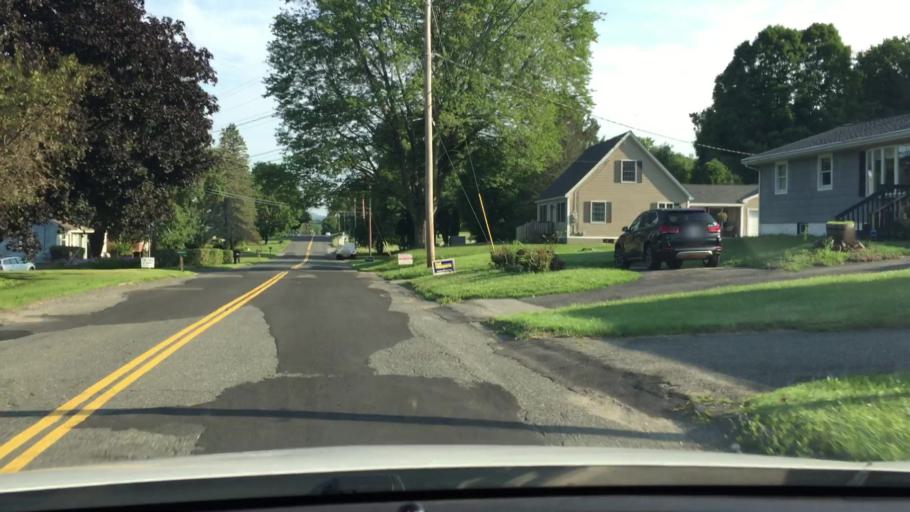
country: US
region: Massachusetts
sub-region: Berkshire County
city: Lee
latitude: 42.3098
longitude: -73.2319
